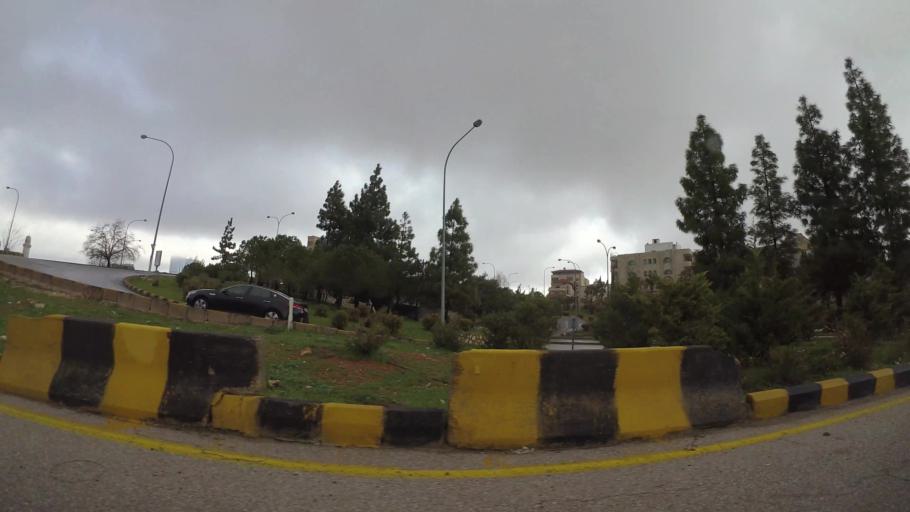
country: JO
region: Amman
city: Wadi as Sir
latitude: 31.9449
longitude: 35.8587
